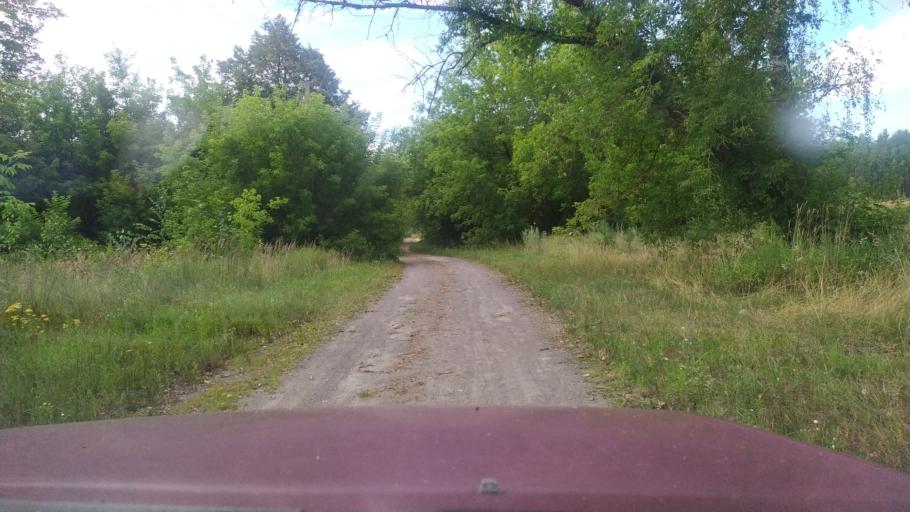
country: RU
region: Brjansk
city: Lyubovsho
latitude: 52.7489
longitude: 31.4606
